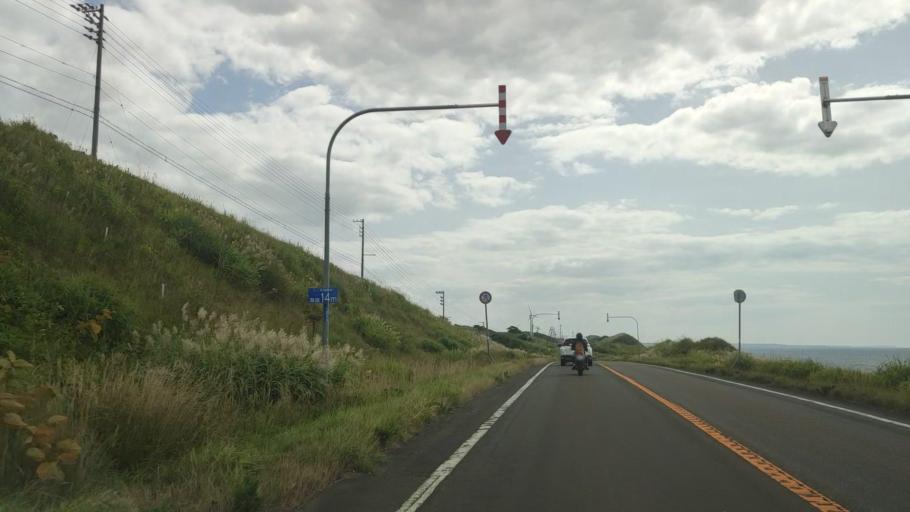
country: JP
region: Hokkaido
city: Rumoi
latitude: 44.5032
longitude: 141.7648
